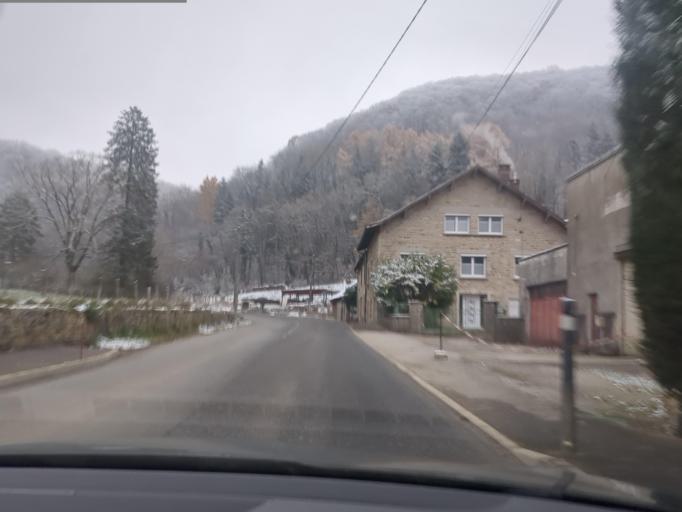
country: FR
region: Franche-Comte
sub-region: Departement du Jura
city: Perrigny
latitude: 46.6333
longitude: 5.6094
